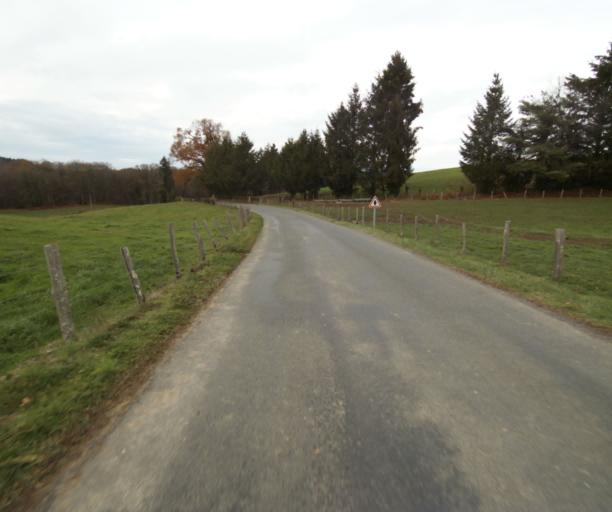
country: FR
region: Limousin
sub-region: Departement de la Correze
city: Chameyrat
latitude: 45.2573
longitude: 1.6790
